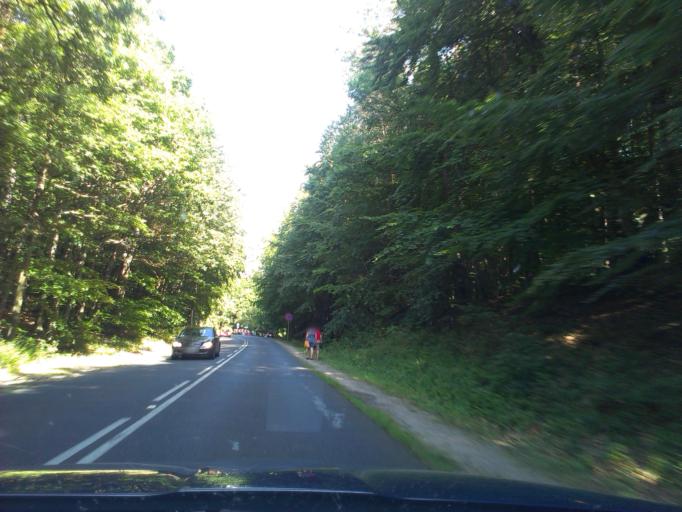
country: PL
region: West Pomeranian Voivodeship
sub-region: Powiat kamienski
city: Miedzyzdroje
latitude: 53.9379
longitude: 14.4731
